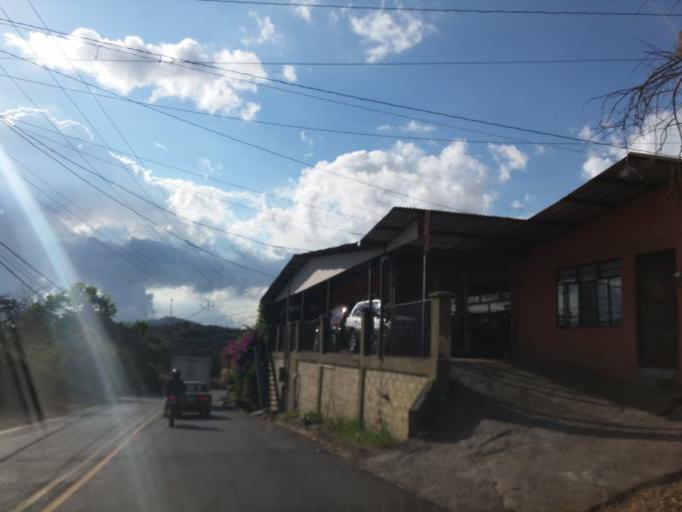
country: CR
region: San Jose
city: San Ignacio
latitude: 9.7958
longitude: -84.1506
